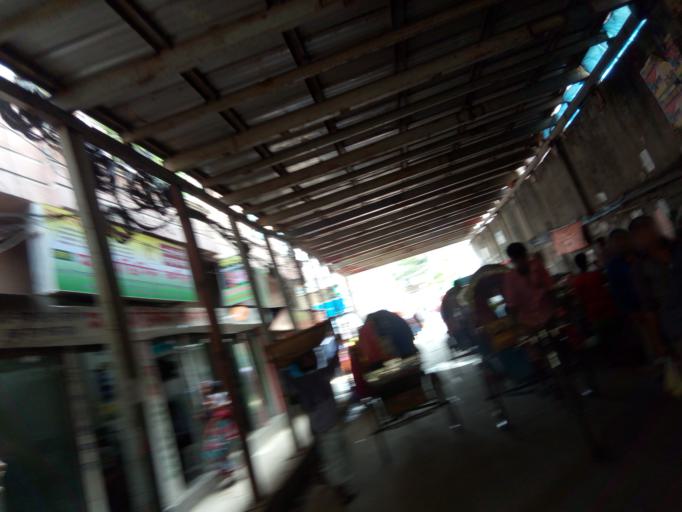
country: BD
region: Dhaka
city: Azimpur
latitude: 23.7517
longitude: 90.3911
